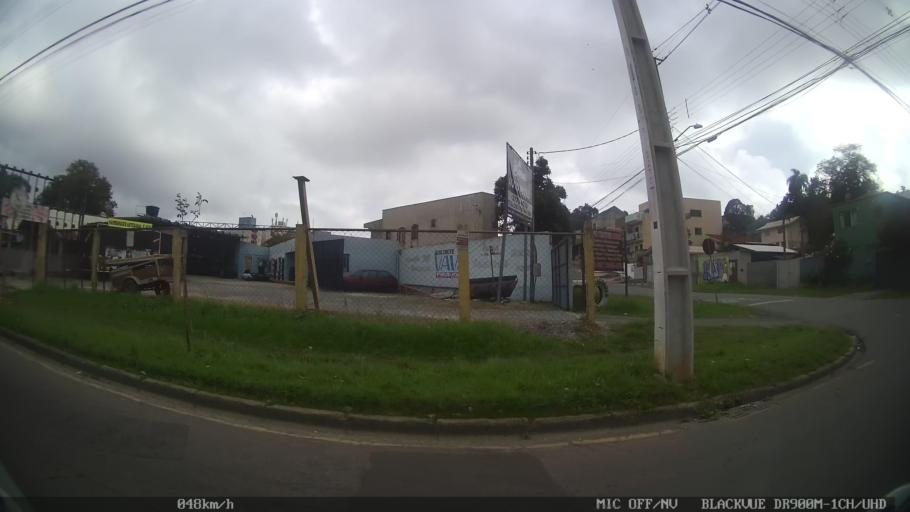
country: BR
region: Parana
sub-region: Curitiba
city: Curitiba
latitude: -25.3798
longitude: -49.2294
